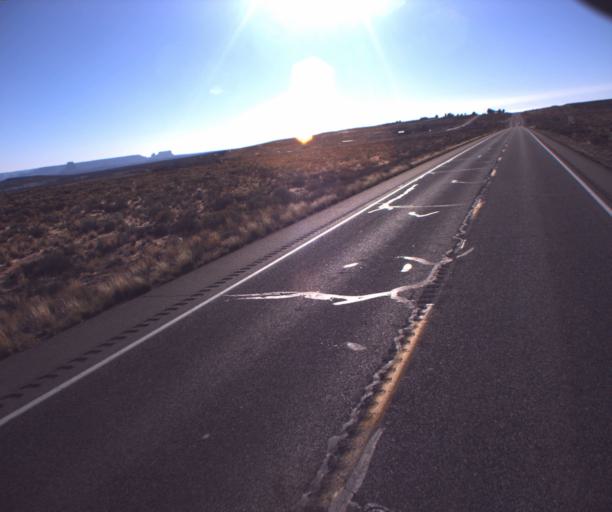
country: US
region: Arizona
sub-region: Coconino County
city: Page
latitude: 37.0000
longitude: -111.5710
